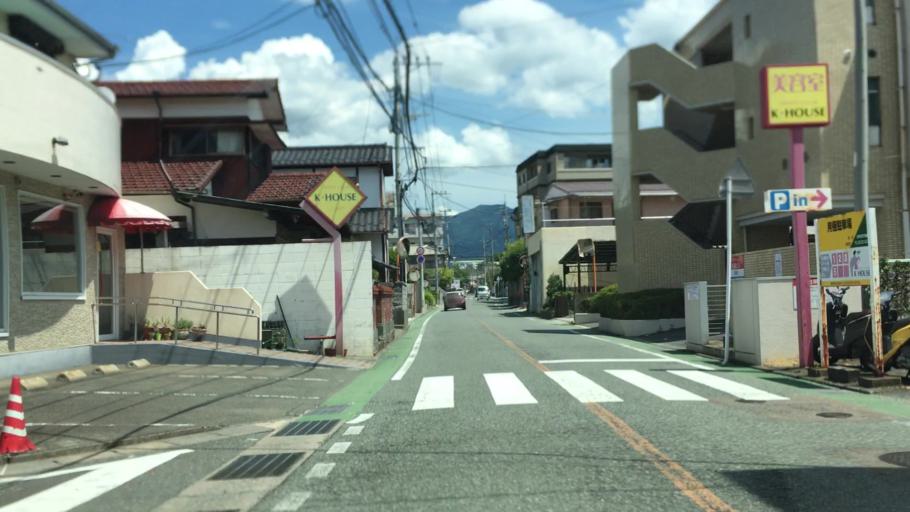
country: JP
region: Fukuoka
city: Dazaifu
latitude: 33.5158
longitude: 130.5271
